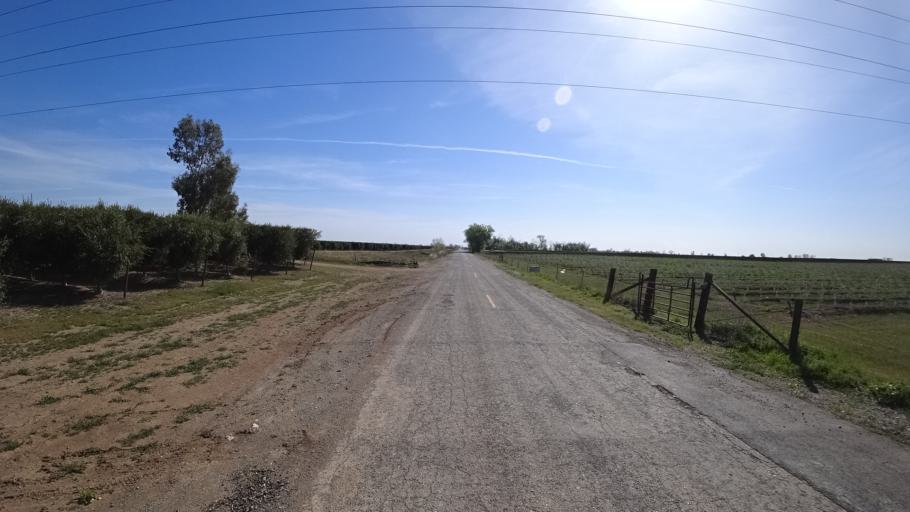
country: US
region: California
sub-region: Glenn County
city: Willows
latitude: 39.6116
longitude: -122.2645
